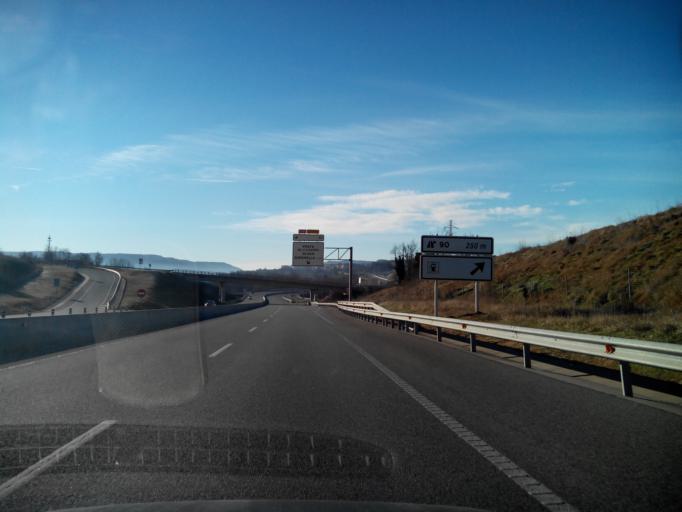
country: ES
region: Catalonia
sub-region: Provincia de Barcelona
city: Gironella
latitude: 42.0488
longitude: 1.8752
